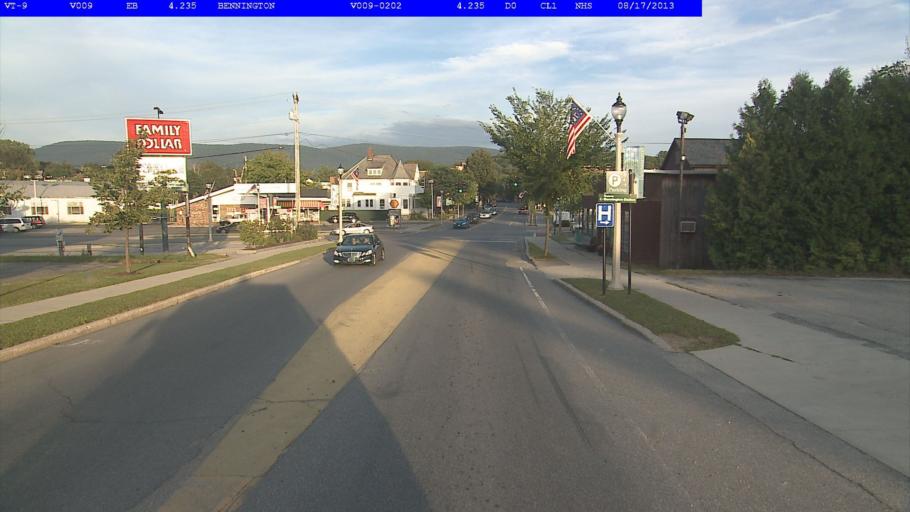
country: US
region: Vermont
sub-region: Bennington County
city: Bennington
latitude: 42.8796
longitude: -73.1997
